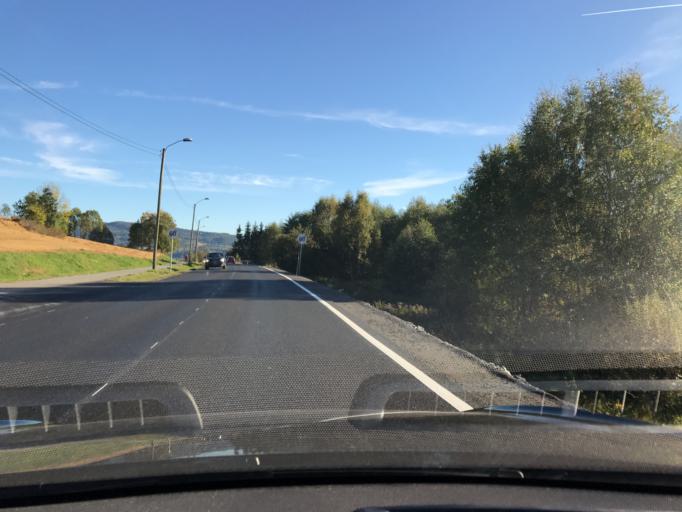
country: NO
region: Buskerud
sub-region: Ovre Eiker
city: Hokksund
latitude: 59.7654
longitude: 9.9650
